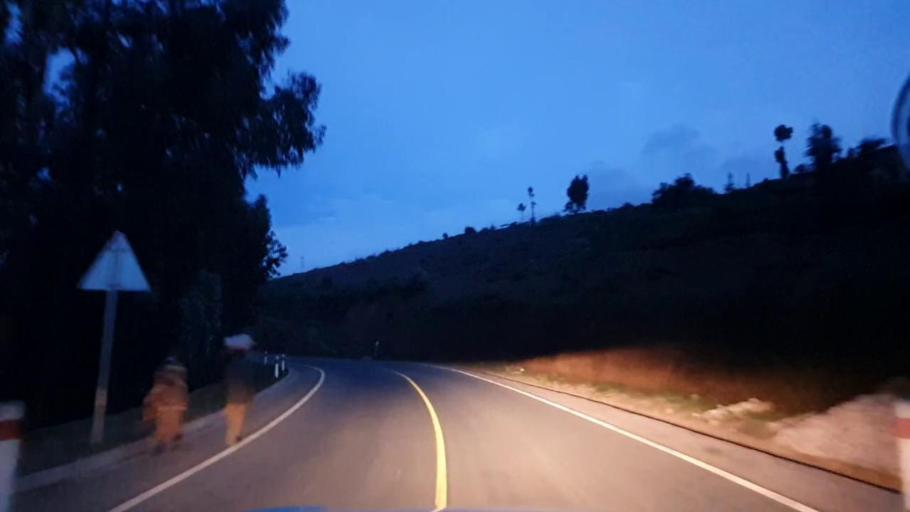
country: RW
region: Southern Province
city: Gikongoro
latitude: -2.4658
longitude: 29.5677
